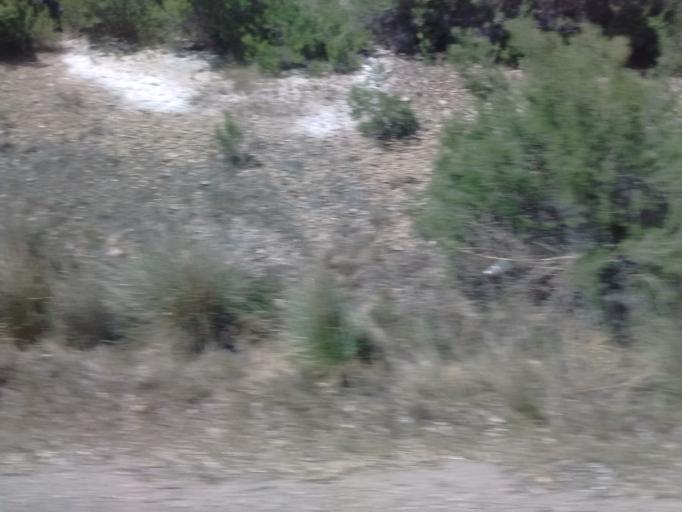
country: US
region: Colorado
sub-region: Mesa County
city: Redlands
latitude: 39.0868
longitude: -108.6267
